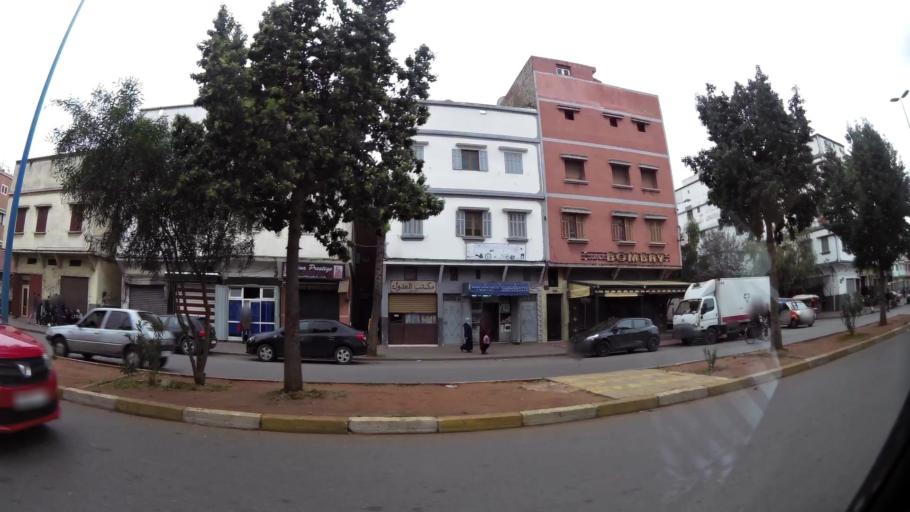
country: MA
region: Grand Casablanca
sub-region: Casablanca
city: Casablanca
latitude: 33.5660
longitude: -7.5674
